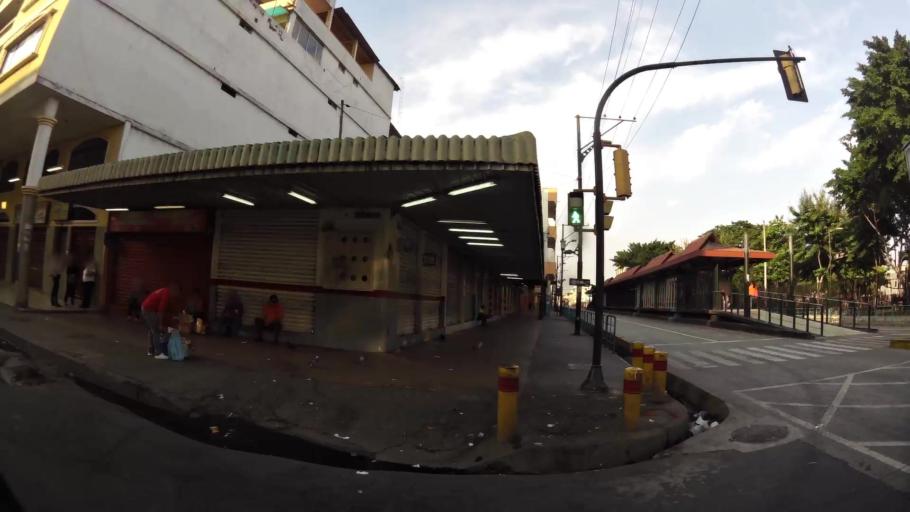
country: EC
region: Guayas
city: Guayaquil
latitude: -2.1931
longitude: -79.8894
